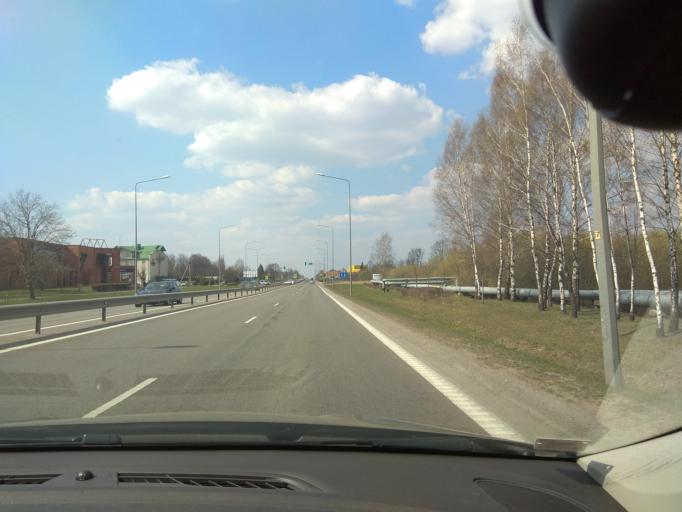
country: LT
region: Siauliu apskritis
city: Radviliskis
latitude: 55.8218
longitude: 23.5316
